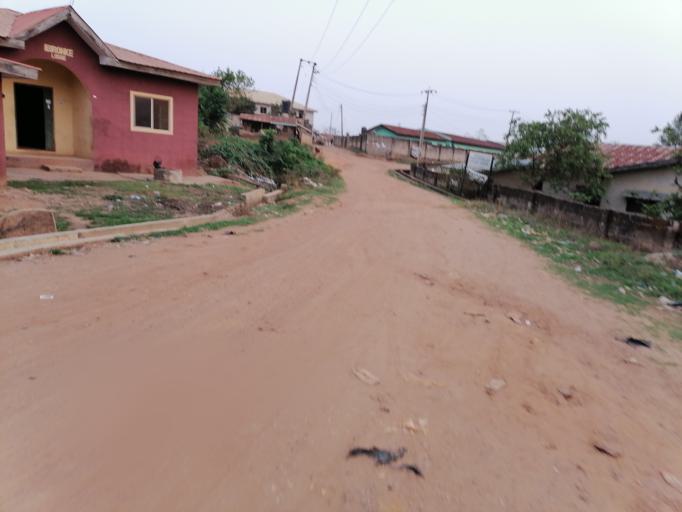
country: NG
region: Ondo
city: Akure
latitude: 7.2877
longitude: 5.1493
